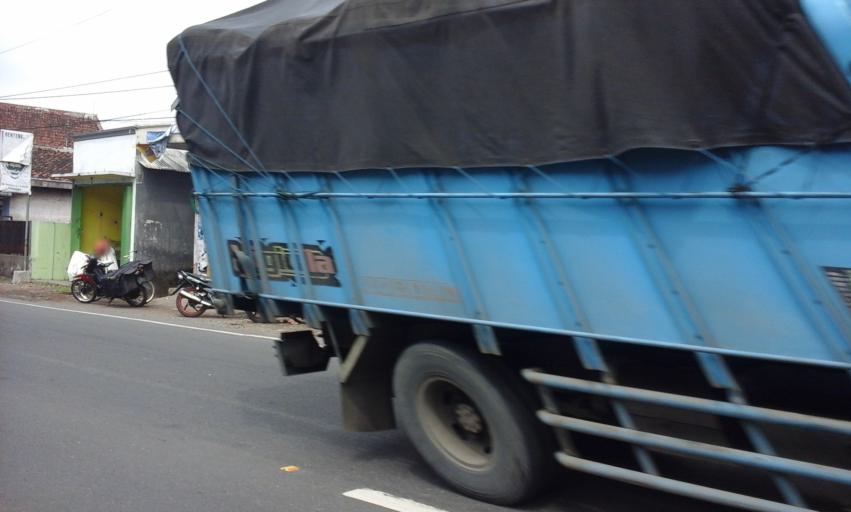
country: ID
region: East Java
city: Mangli
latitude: -8.1903
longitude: 113.6513
